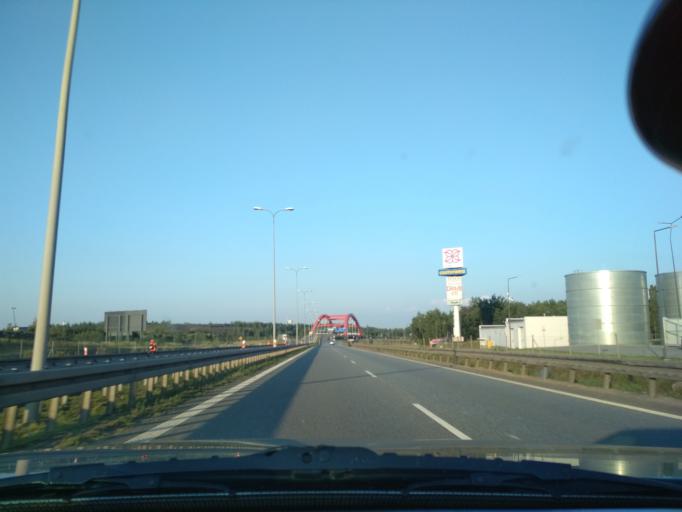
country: PL
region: Silesian Voivodeship
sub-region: Powiat gliwicki
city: Przyszowice
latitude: 50.2685
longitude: 18.7207
